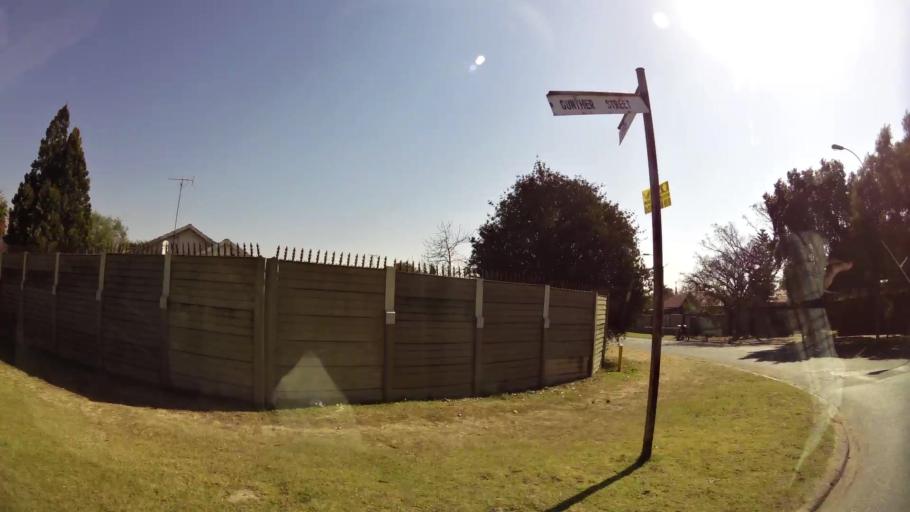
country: ZA
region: Gauteng
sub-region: Ekurhuleni Metropolitan Municipality
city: Tembisa
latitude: -26.0456
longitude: 28.2269
